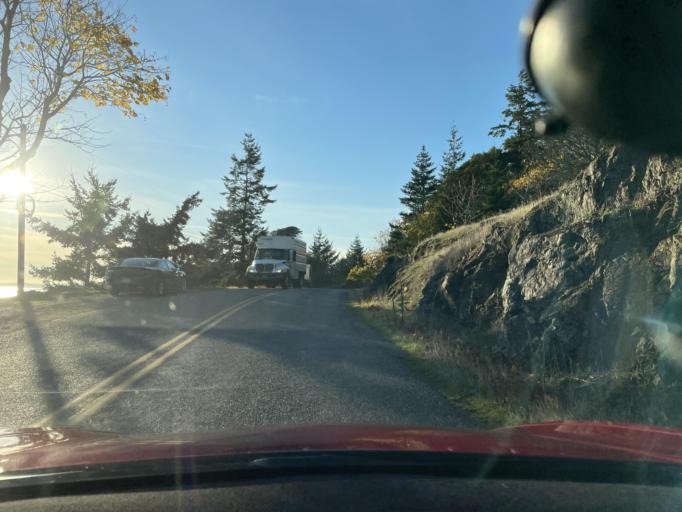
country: US
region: Washington
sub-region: San Juan County
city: Friday Harbor
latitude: 48.5140
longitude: -123.1473
